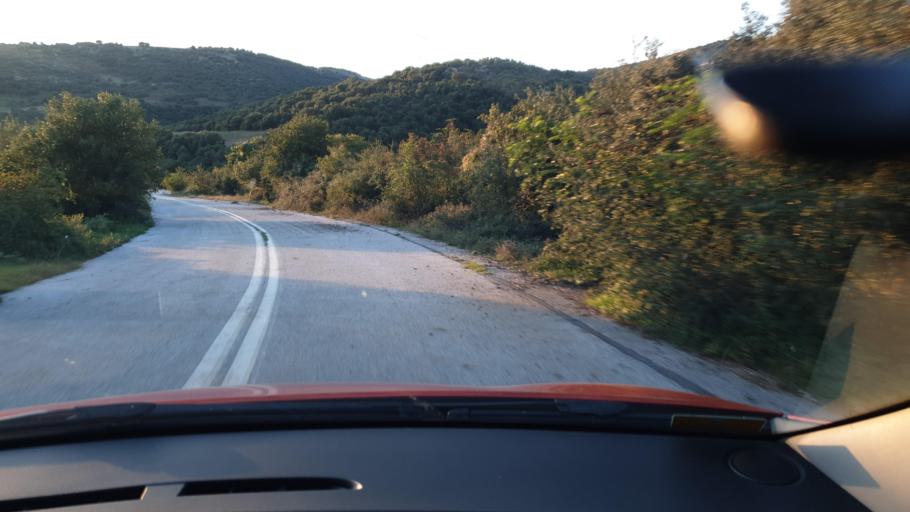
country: GR
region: Central Macedonia
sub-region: Nomos Chalkidikis
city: Galatista
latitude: 40.4579
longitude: 23.3108
